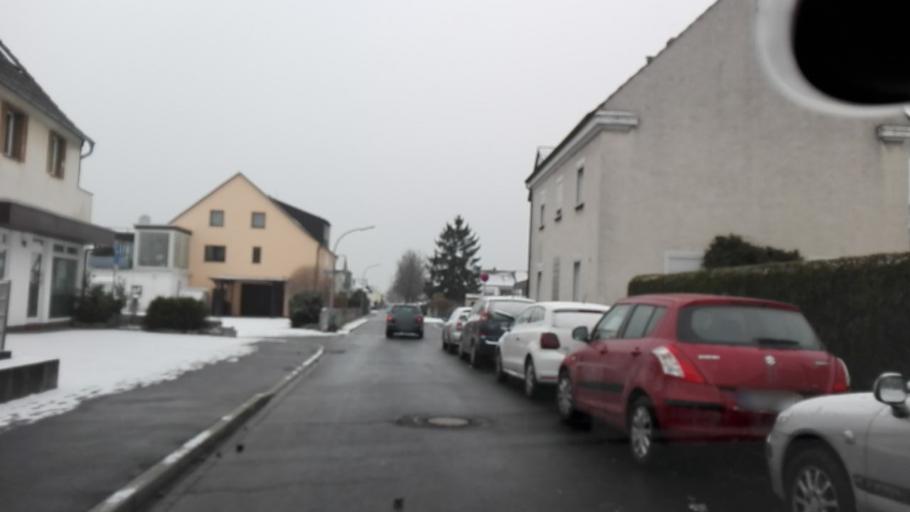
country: DE
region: North Rhine-Westphalia
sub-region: Regierungsbezirk Arnsberg
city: Unna
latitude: 51.5393
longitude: 7.6495
